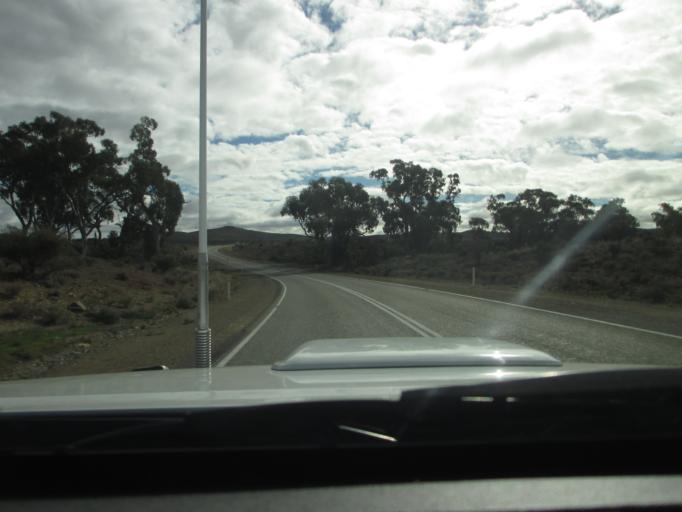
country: AU
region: South Australia
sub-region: Flinders Ranges
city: Quorn
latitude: -32.2816
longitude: 138.4950
